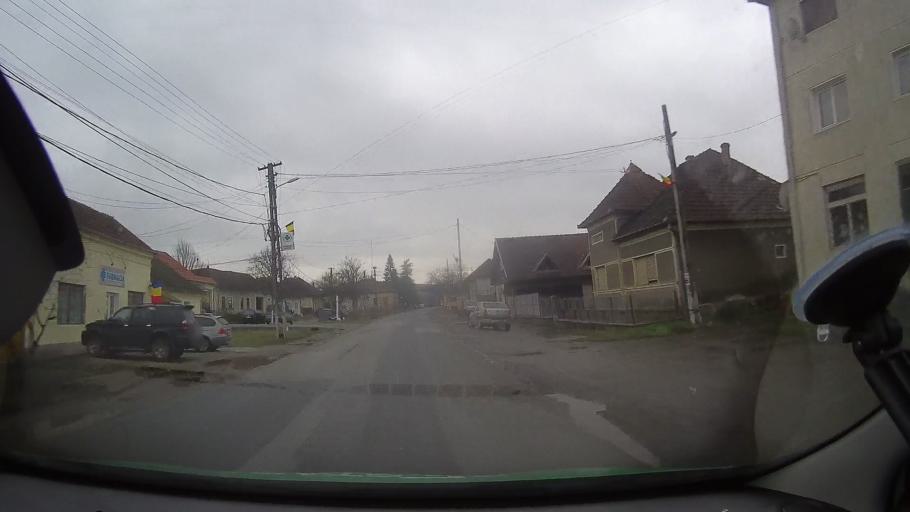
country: RO
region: Arad
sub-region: Comuna Halmagiu
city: Halmagiu
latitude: 46.2689
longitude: 22.5967
